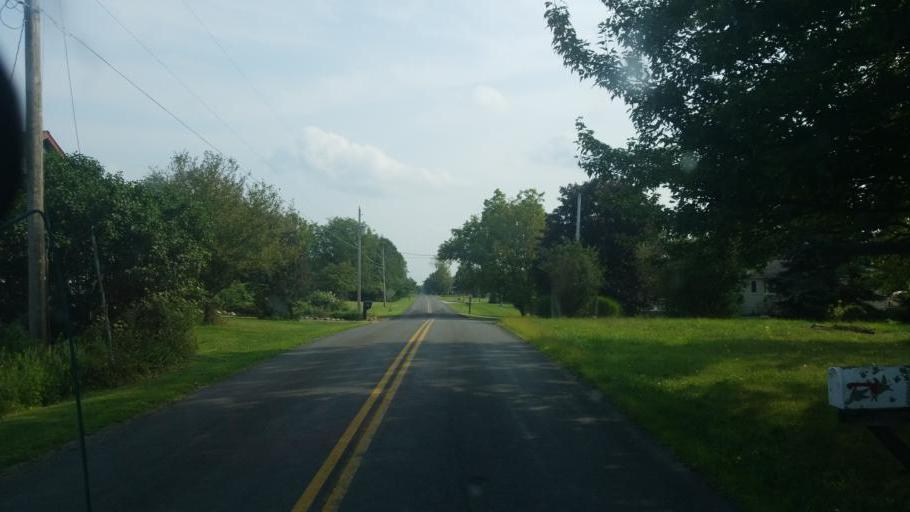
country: US
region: Ohio
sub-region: Medina County
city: Medina
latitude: 41.0759
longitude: -81.8850
